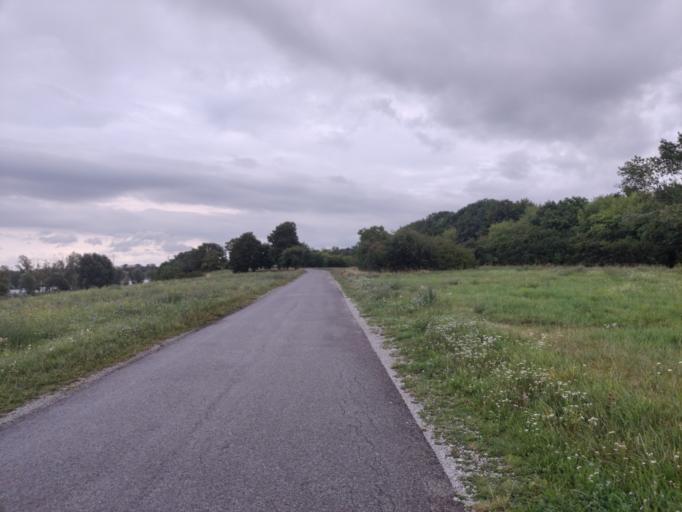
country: AT
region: Lower Austria
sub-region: Politischer Bezirk Korneuburg
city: Langenzersdorf
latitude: 48.2754
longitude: 16.3636
